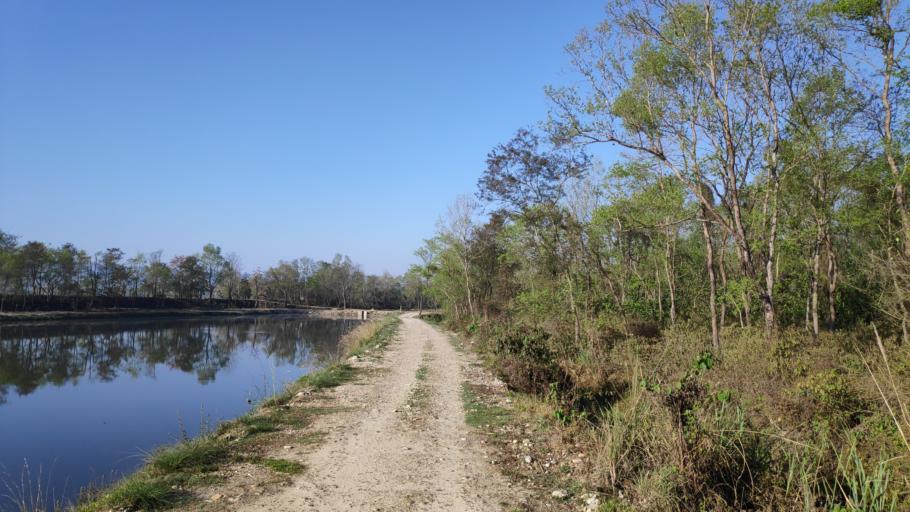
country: NP
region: Central Region
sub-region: Narayani Zone
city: Bharatpur
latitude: 27.5619
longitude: 84.5736
